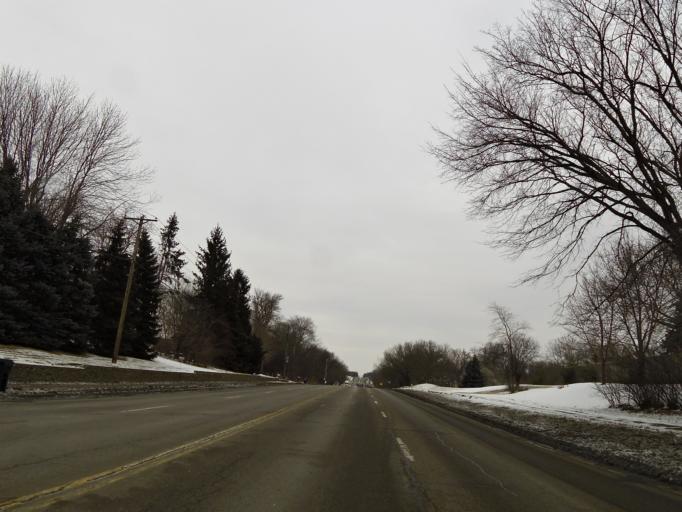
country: US
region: Minnesota
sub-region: Scott County
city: Savage
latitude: 44.8139
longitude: -93.3504
